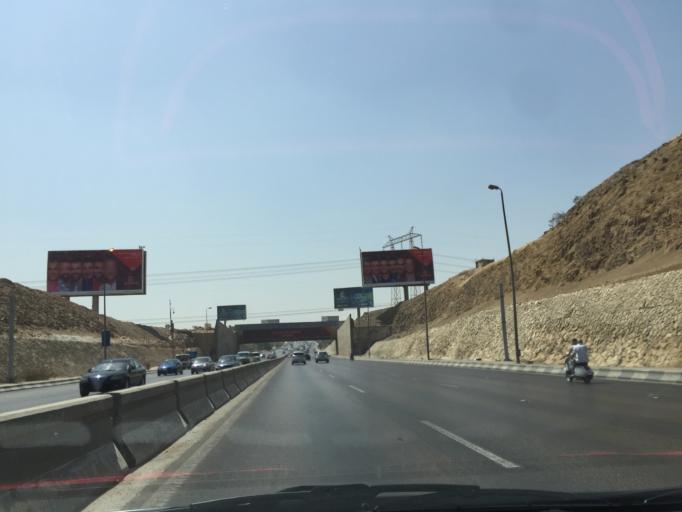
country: EG
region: Al Jizah
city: Awsim
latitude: 30.0565
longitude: 31.0761
